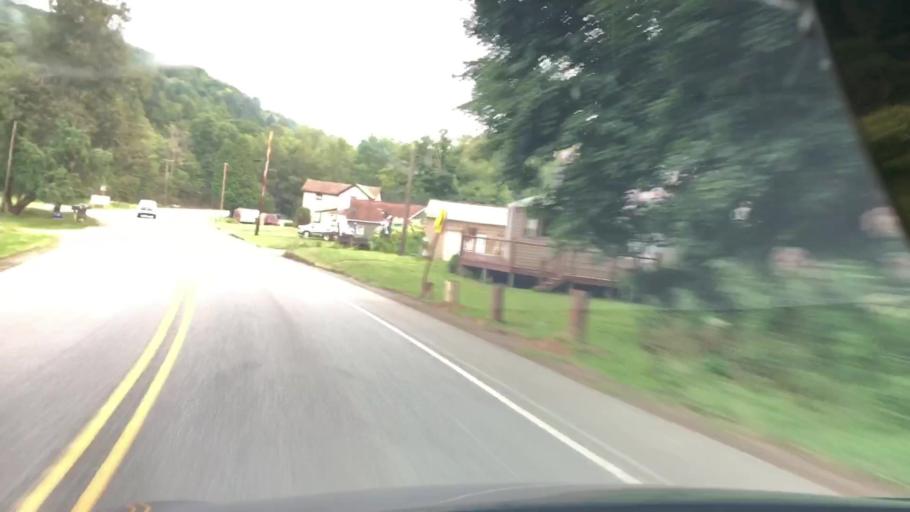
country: US
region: Pennsylvania
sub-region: Venango County
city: Hasson Heights
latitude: 41.4977
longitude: -79.7013
